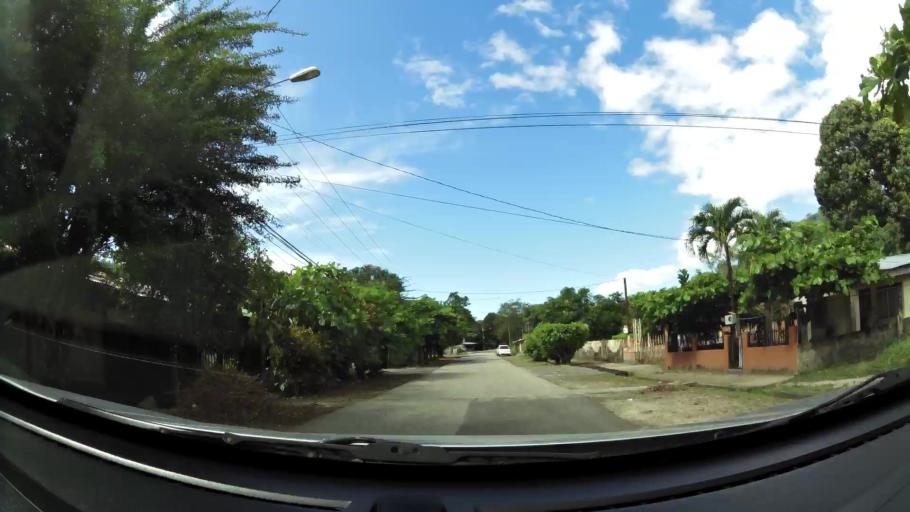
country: CR
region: Guanacaste
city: Juntas
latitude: 10.2807
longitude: -84.9440
